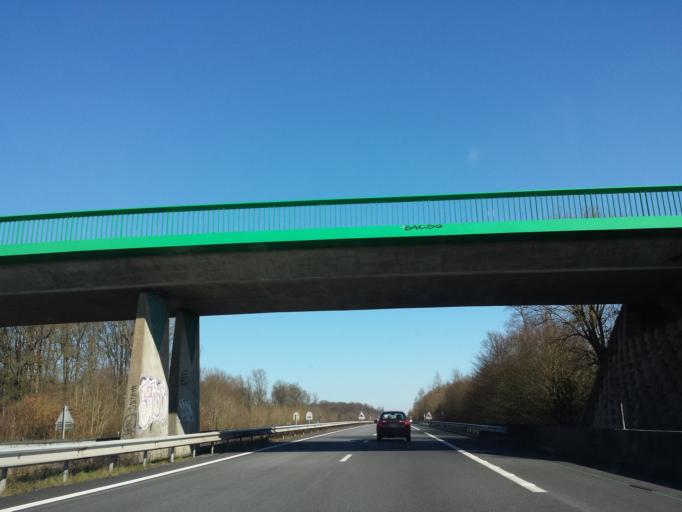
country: FR
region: Picardie
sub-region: Departement de l'Oise
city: Saint-Crepin-Ibouvillers
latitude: 49.3138
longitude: 2.0819
